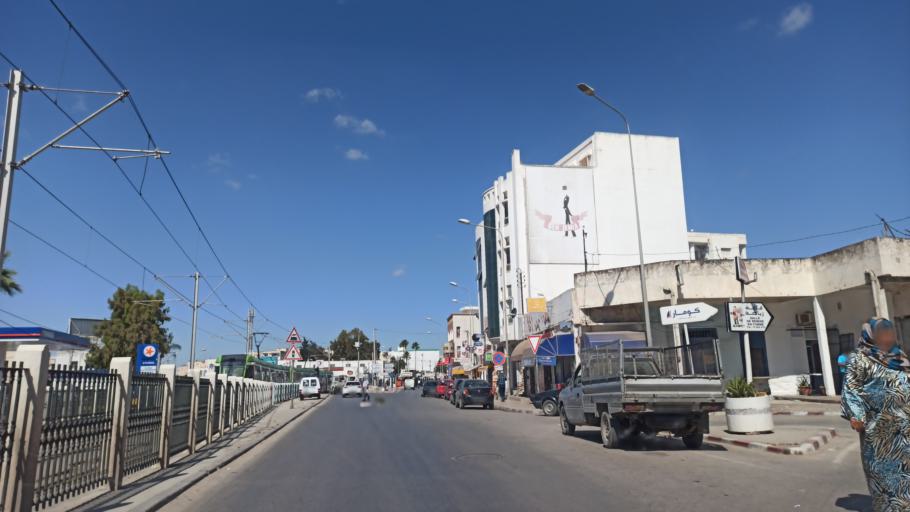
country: TN
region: Manouba
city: Manouba
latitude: 36.8025
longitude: 10.1129
